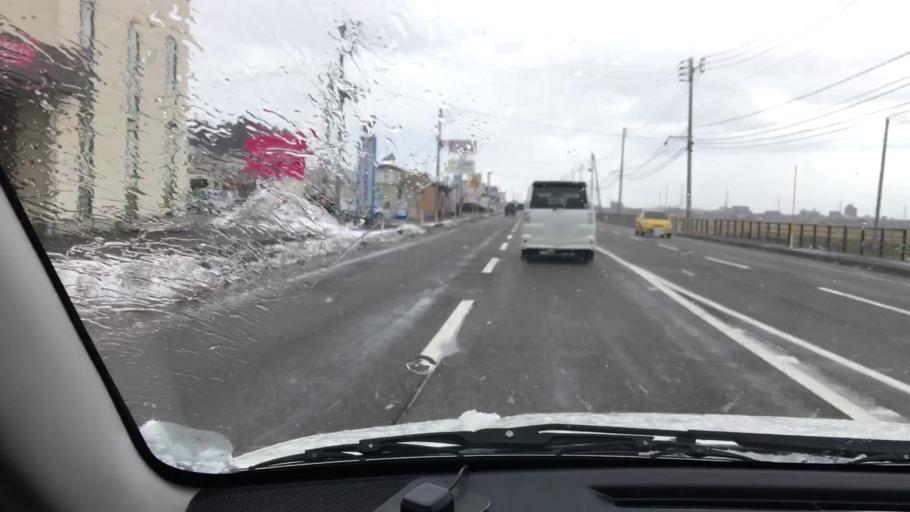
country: JP
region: Niigata
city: Joetsu
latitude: 37.1246
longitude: 138.2321
